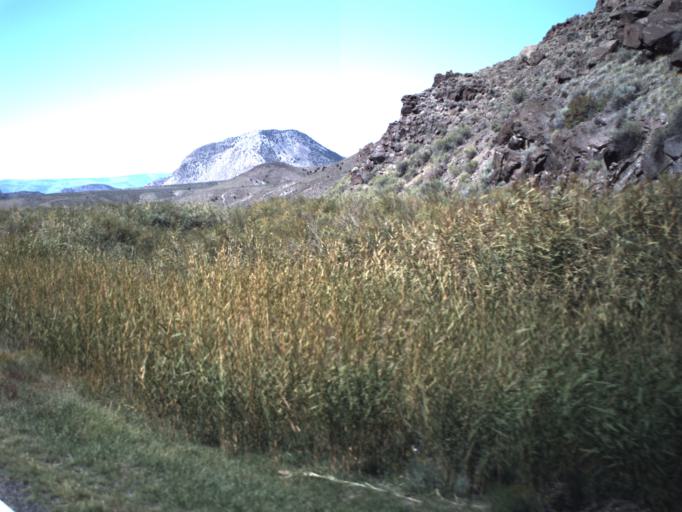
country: US
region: Utah
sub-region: Piute County
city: Junction
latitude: 38.1650
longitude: -112.0321
